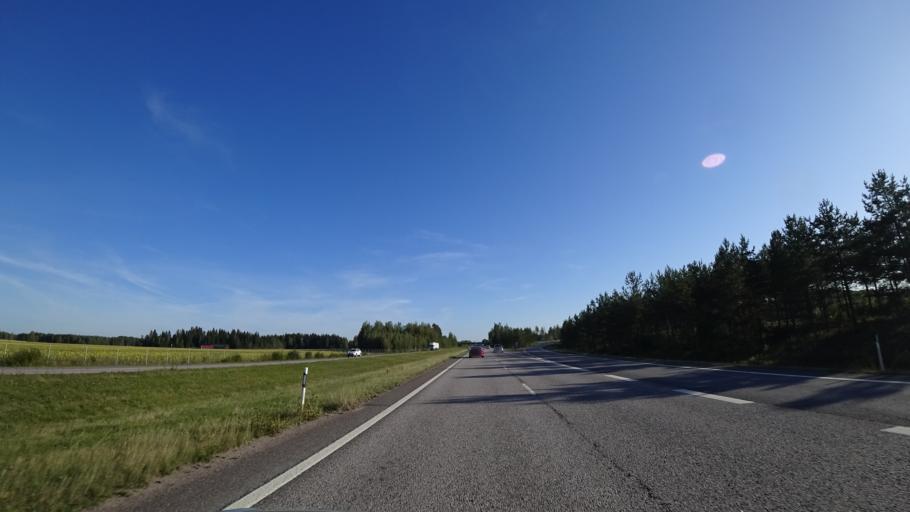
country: FI
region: Uusimaa
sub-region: Helsinki
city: Nurmijaervi
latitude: 60.5223
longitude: 24.8445
